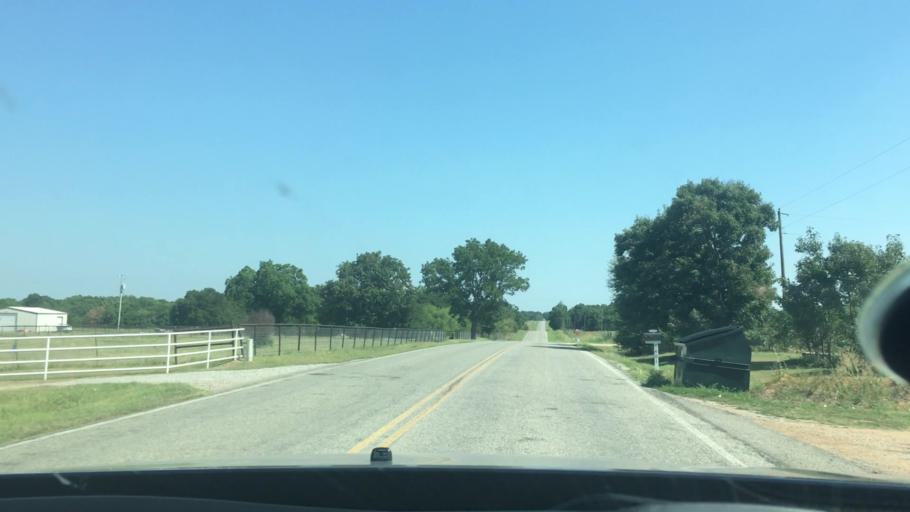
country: US
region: Oklahoma
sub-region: Johnston County
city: Tishomingo
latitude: 34.2677
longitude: -96.6186
